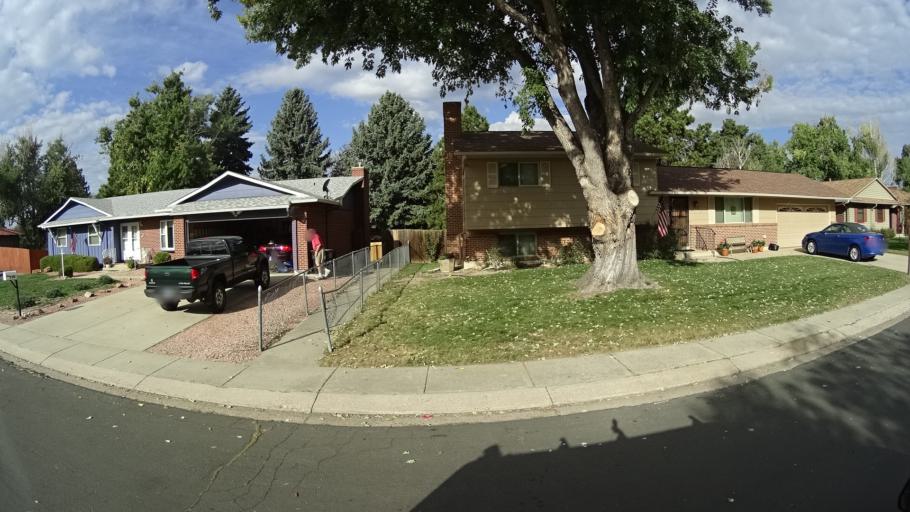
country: US
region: Colorado
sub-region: El Paso County
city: Cimarron Hills
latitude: 38.8646
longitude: -104.7512
